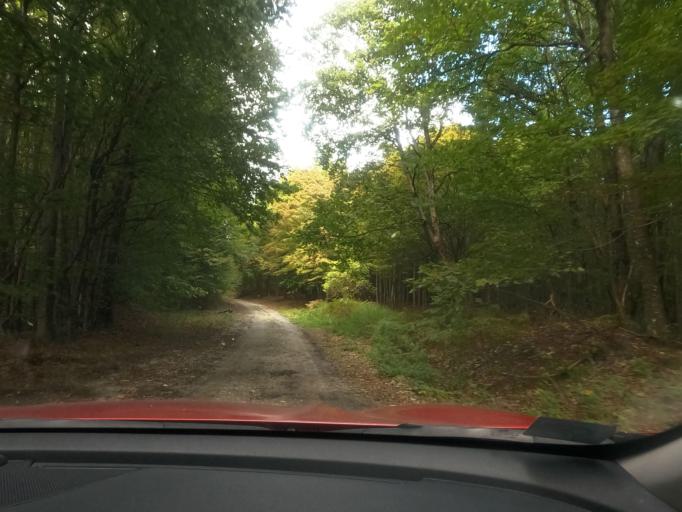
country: BA
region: Federation of Bosnia and Herzegovina
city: Velika Kladusa
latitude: 45.2640
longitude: 15.7823
